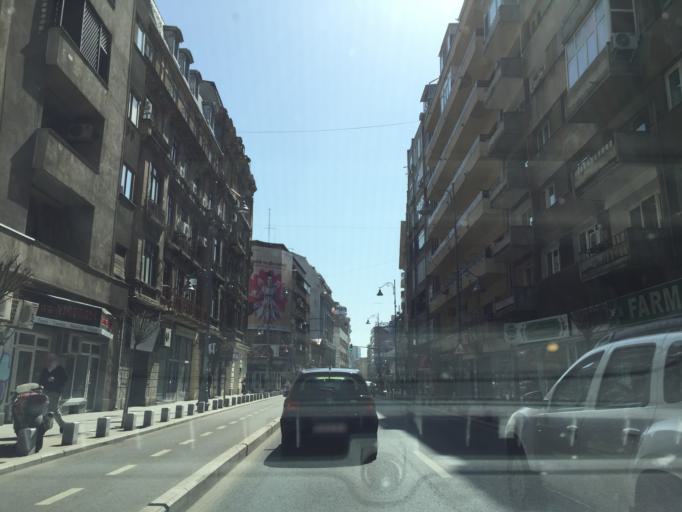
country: RO
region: Bucuresti
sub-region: Municipiul Bucuresti
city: Bucuresti
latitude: 44.4438
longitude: 26.0926
